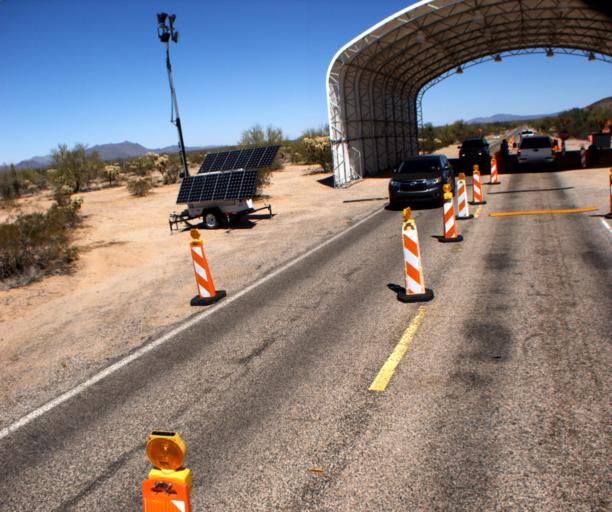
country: US
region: Arizona
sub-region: Pima County
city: Ajo
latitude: 32.2021
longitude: -112.7592
